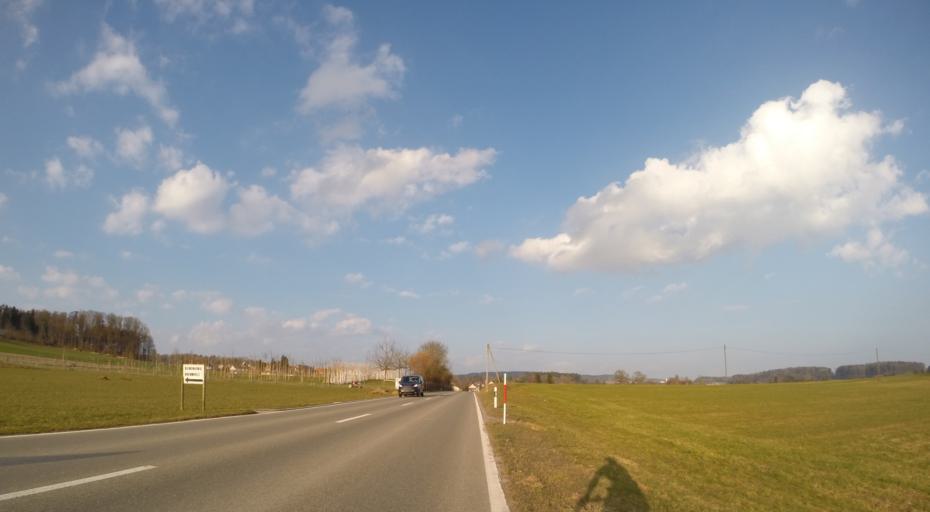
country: CH
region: Thurgau
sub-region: Frauenfeld District
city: Pfyn
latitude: 47.6283
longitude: 8.9627
